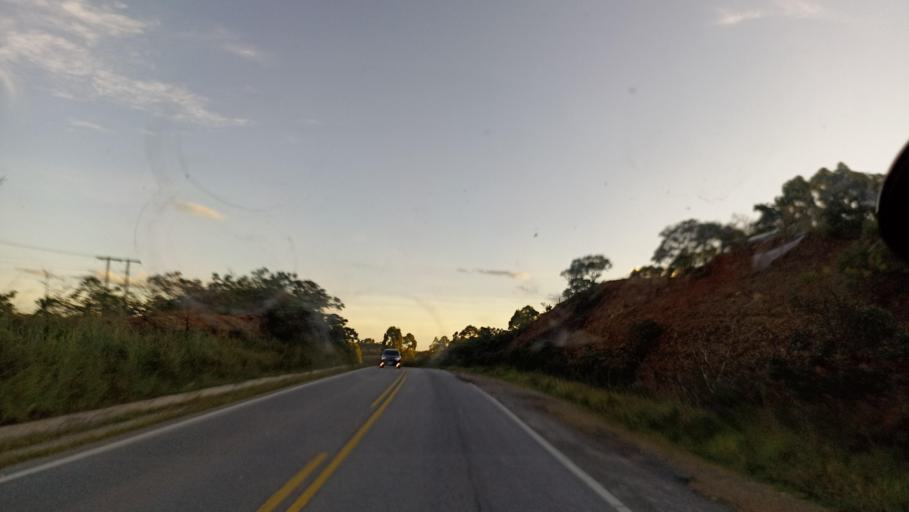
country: BR
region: Minas Gerais
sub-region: Sao Joao Del Rei
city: Sao Joao del Rei
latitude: -21.2194
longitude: -44.3596
